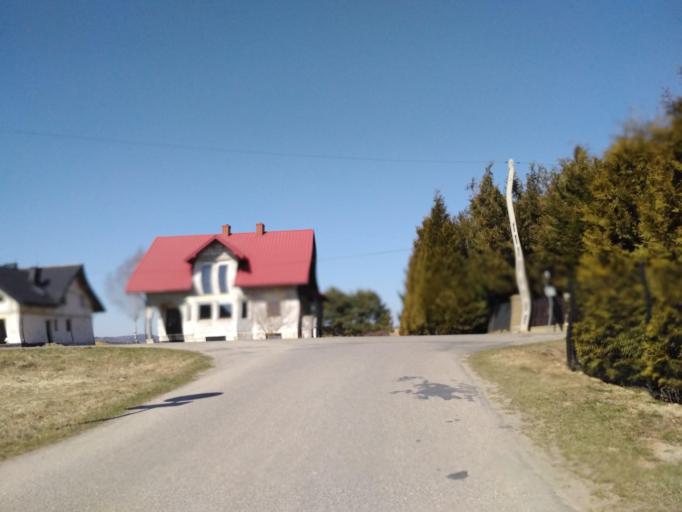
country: PL
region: Subcarpathian Voivodeship
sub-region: Powiat brzozowski
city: Orzechowka
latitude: 49.7178
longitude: 21.9626
